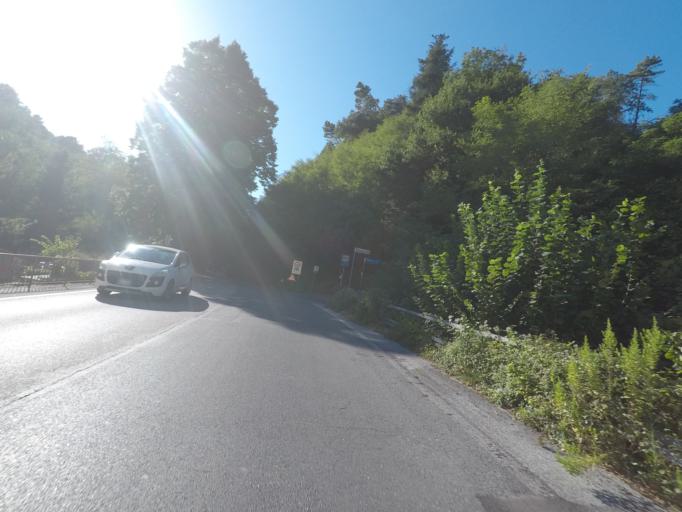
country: IT
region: Tuscany
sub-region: Provincia di Lucca
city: Massarosa
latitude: 43.9036
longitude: 10.3736
